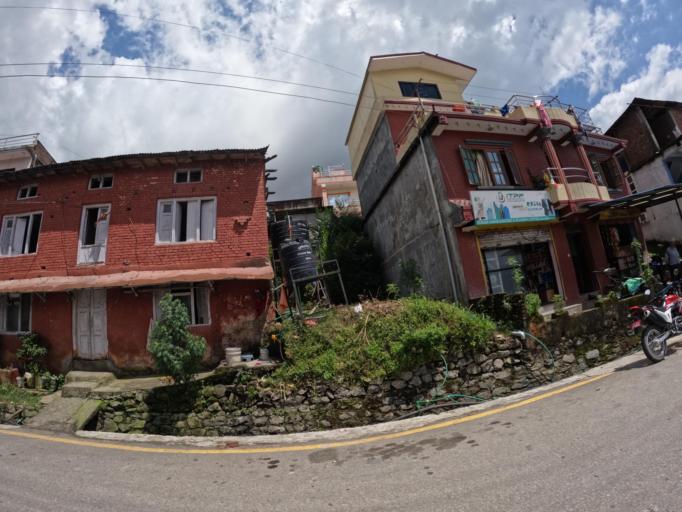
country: NP
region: Central Region
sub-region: Bagmati Zone
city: Kathmandu
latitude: 27.7905
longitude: 85.3301
